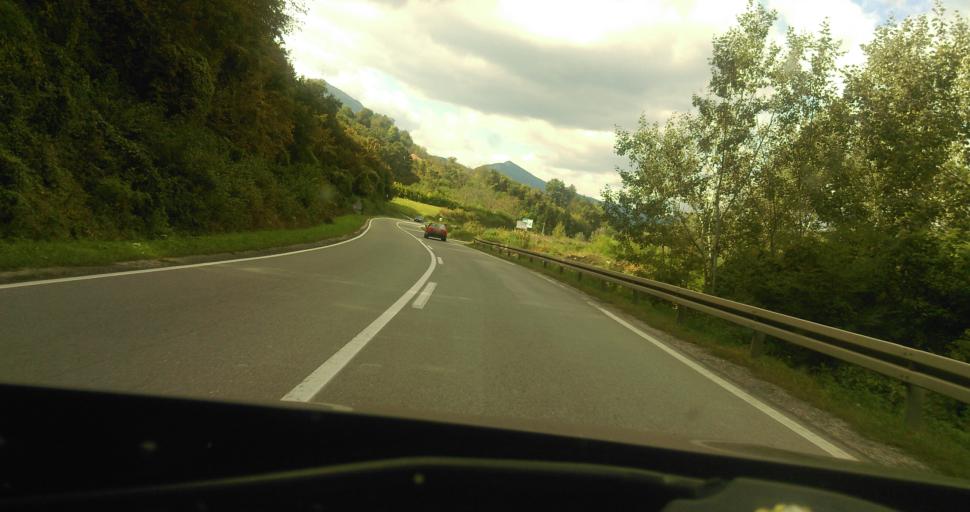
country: RS
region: Central Serbia
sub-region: Moravicki Okrug
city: Cacak
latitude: 43.8965
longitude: 20.2851
